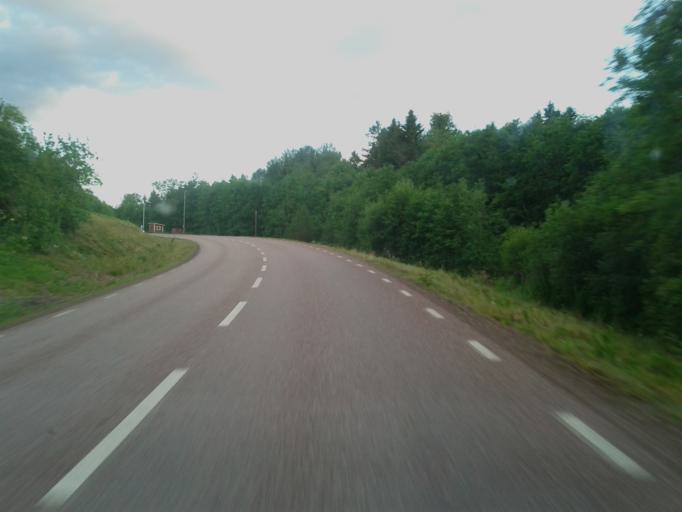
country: SE
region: Dalarna
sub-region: Borlange Kommun
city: Borlaenge
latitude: 60.3870
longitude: 15.3778
